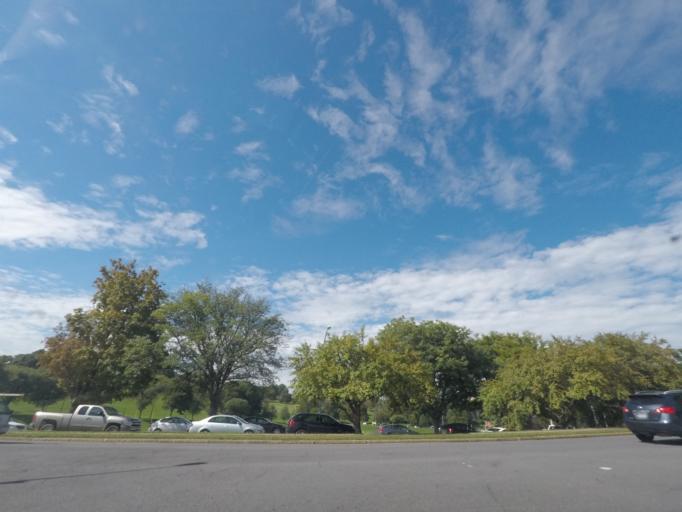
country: US
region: New York
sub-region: Albany County
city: Albany
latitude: 42.6444
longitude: -73.7618
